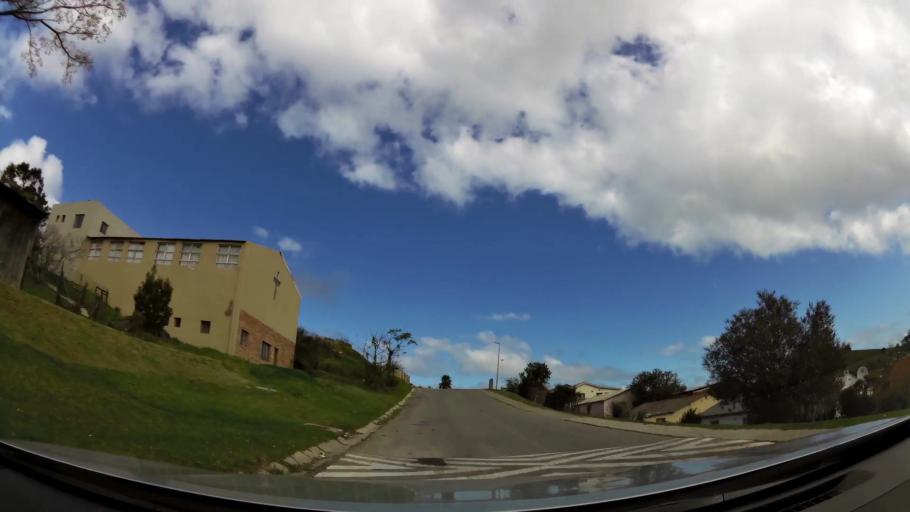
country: ZA
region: Western Cape
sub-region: Eden District Municipality
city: Knysna
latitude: -34.0511
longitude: 23.0965
